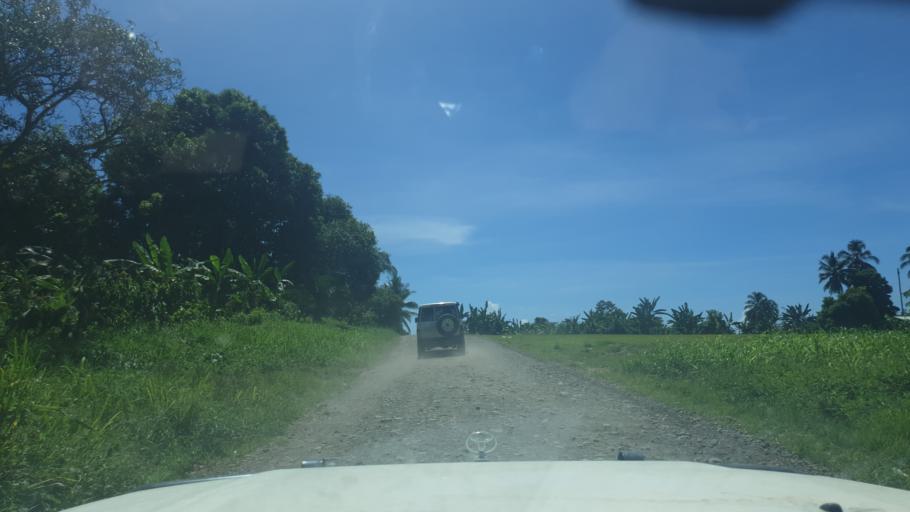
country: PG
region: Bougainville
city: Arawa
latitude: -5.8110
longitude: 155.1492
